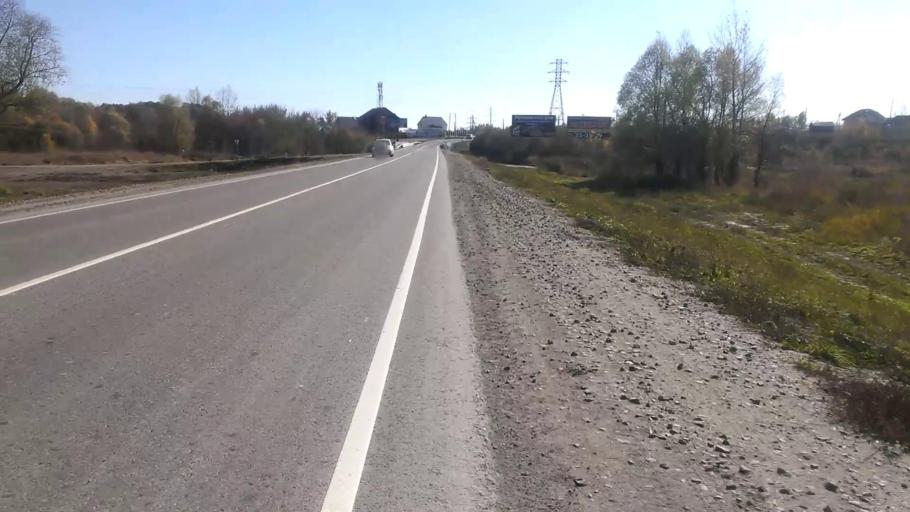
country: RU
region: Altai Krai
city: Sannikovo
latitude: 53.3214
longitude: 83.9429
